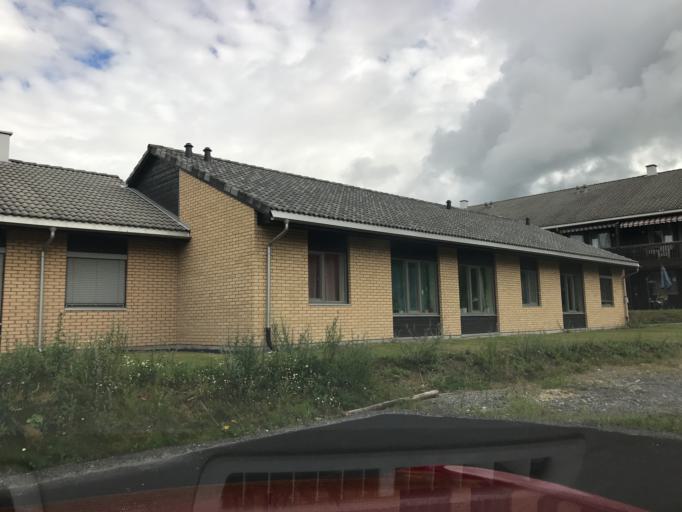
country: NO
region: Buskerud
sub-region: Flesberg
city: Lampeland
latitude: 59.8363
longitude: 9.5794
